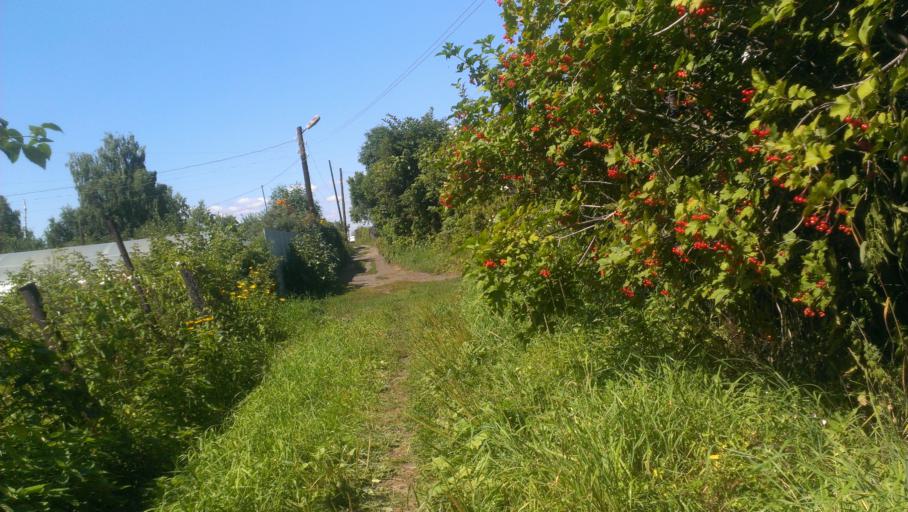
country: RU
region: Altai Krai
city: Nauchnyy Gorodok
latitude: 53.4243
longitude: 83.5067
